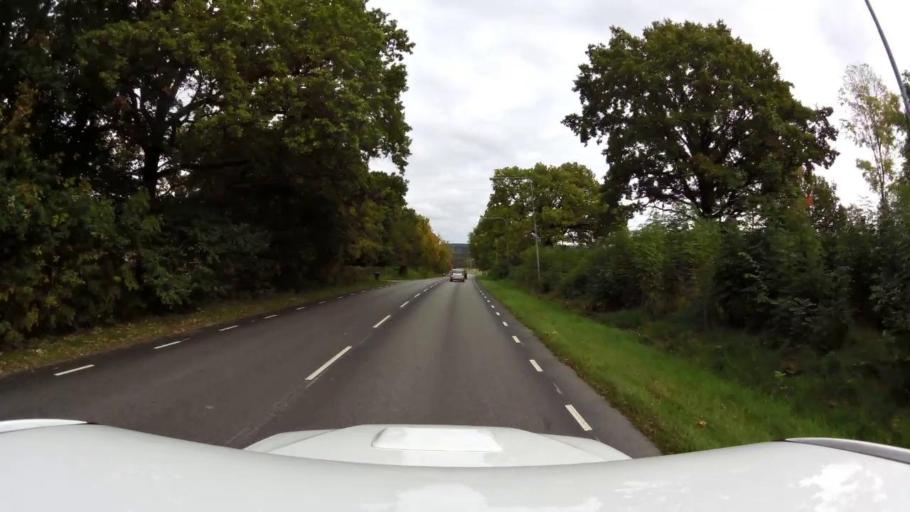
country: SE
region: OEstergoetland
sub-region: Linkopings Kommun
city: Berg
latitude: 58.4924
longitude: 15.5286
